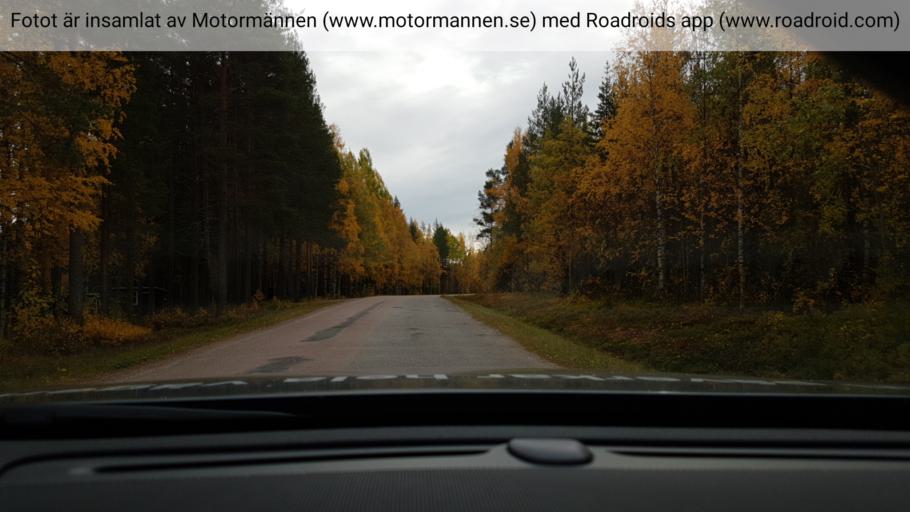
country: SE
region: Norrbotten
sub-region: Overkalix Kommun
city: OEverkalix
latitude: 66.2332
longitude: 23.0121
